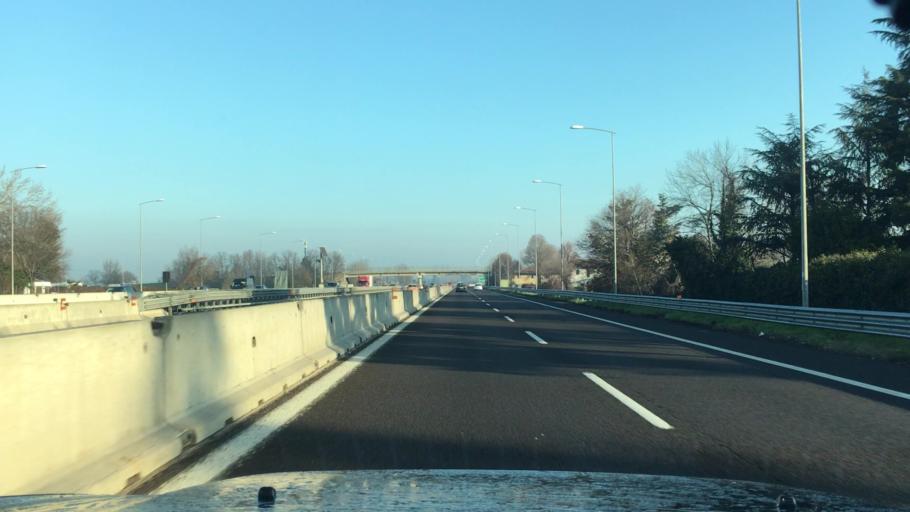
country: IT
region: Emilia-Romagna
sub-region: Provincia di Bologna
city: Casalecchio di Reno
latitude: 44.4992
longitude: 11.2719
